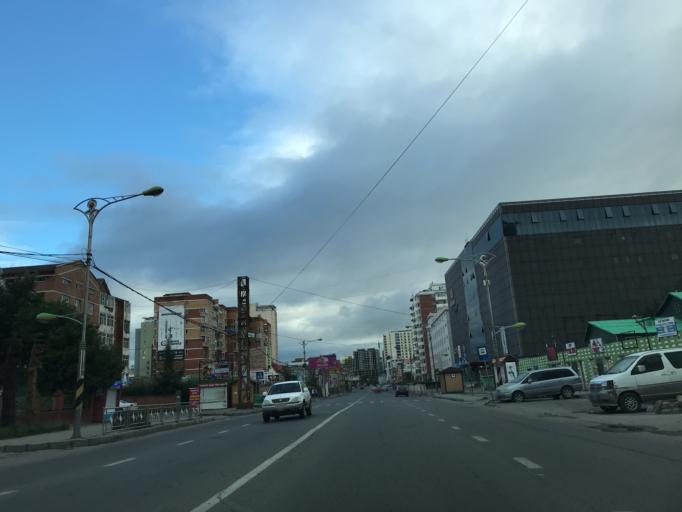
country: MN
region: Ulaanbaatar
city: Ulaanbaatar
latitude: 47.9099
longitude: 106.9435
